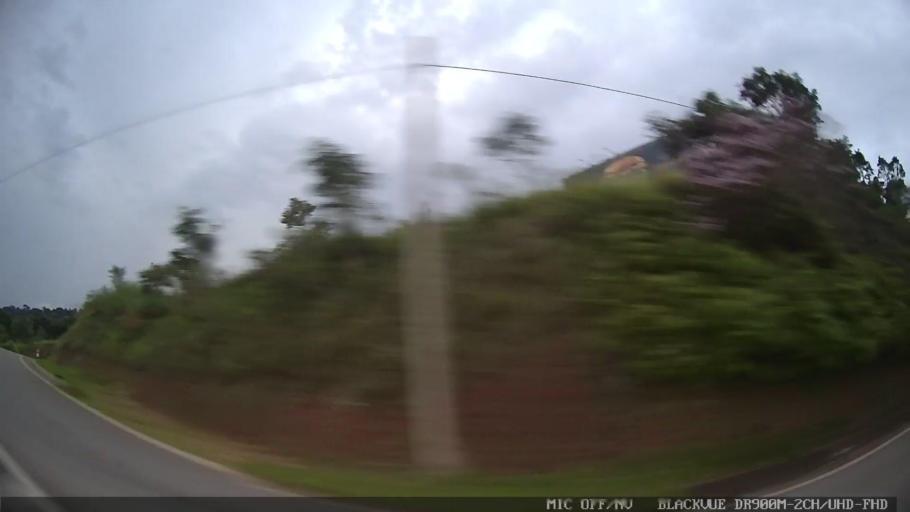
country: BR
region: Sao Paulo
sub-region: Santa Branca
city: Santa Branca
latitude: -23.4379
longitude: -45.6178
